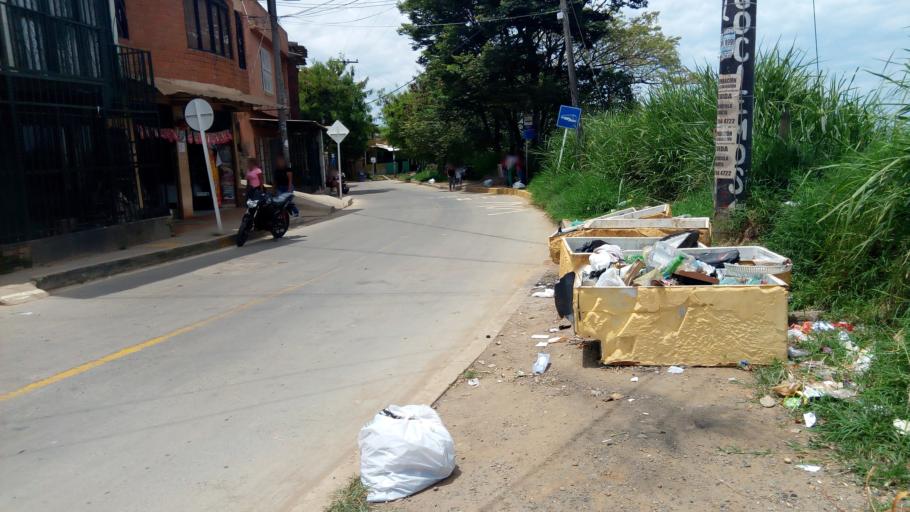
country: CO
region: Valle del Cauca
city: Cali
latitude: 3.3781
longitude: -76.5613
